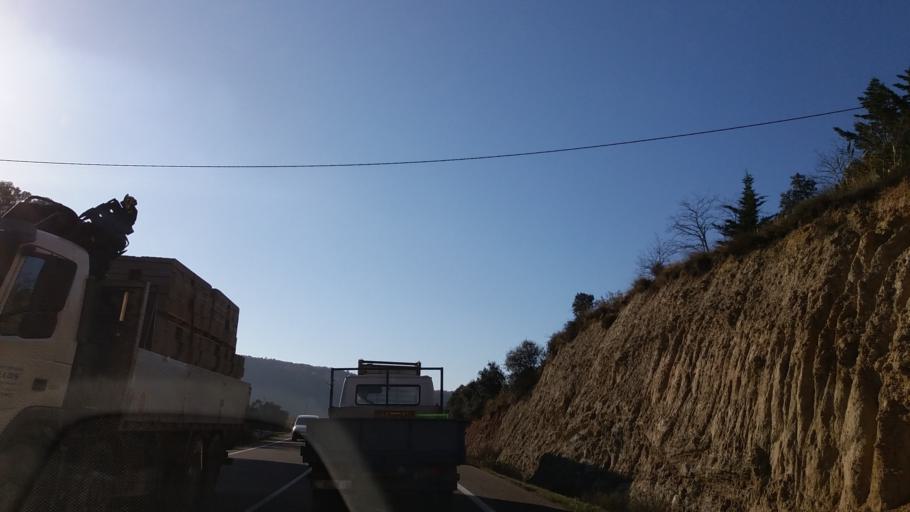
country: ES
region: Catalonia
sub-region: Provincia de Lleida
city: Ponts
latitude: 41.9004
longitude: 1.1690
